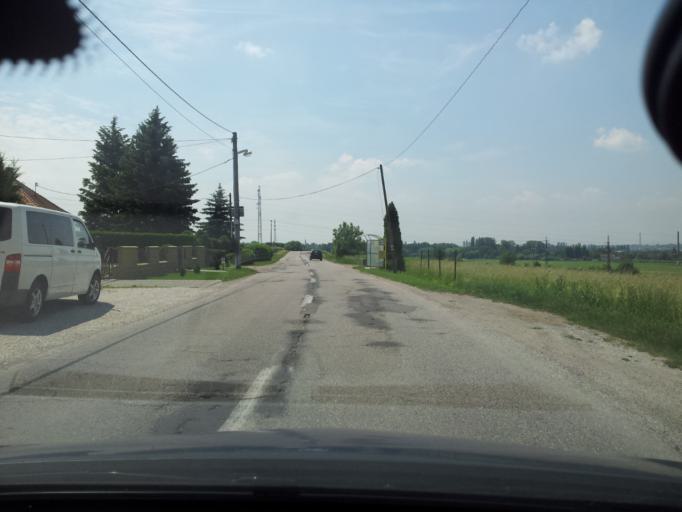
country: SK
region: Nitriansky
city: Zlate Moravce
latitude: 48.3962
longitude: 18.4155
